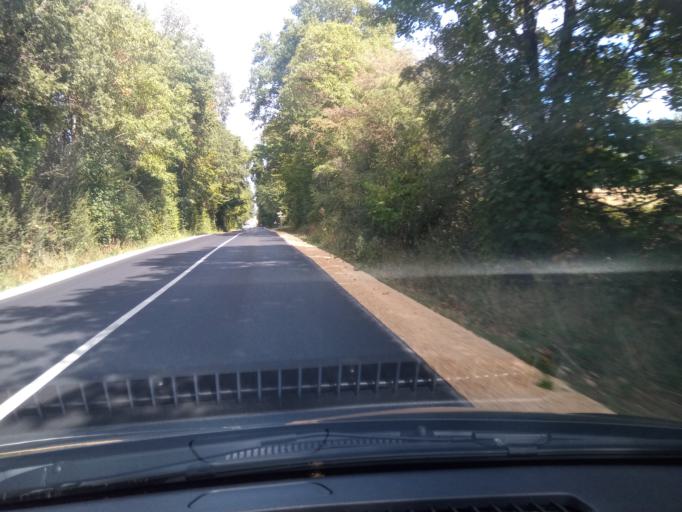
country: FR
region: Poitou-Charentes
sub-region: Departement de la Vienne
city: Terce
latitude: 46.4851
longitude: 0.5372
